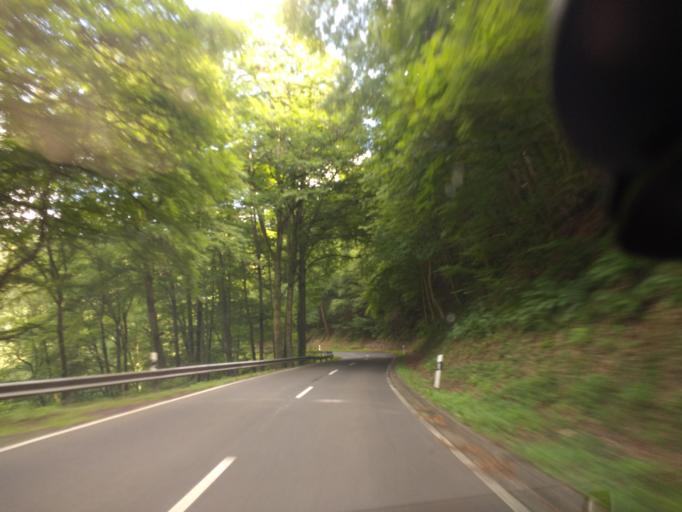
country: DE
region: Rheinland-Pfalz
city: Berglicht
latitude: 49.8091
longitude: 6.9610
